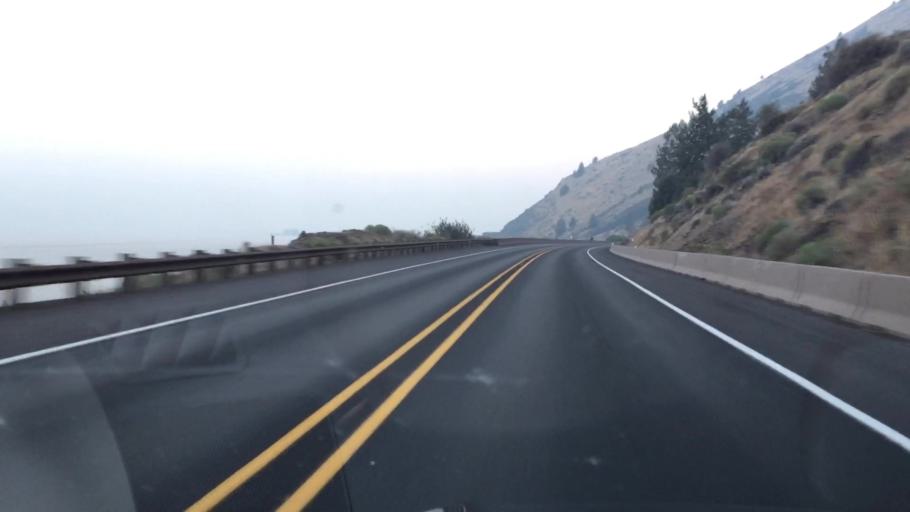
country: US
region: Oregon
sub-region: Klamath County
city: Klamath Falls
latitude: 42.4269
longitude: -121.8534
